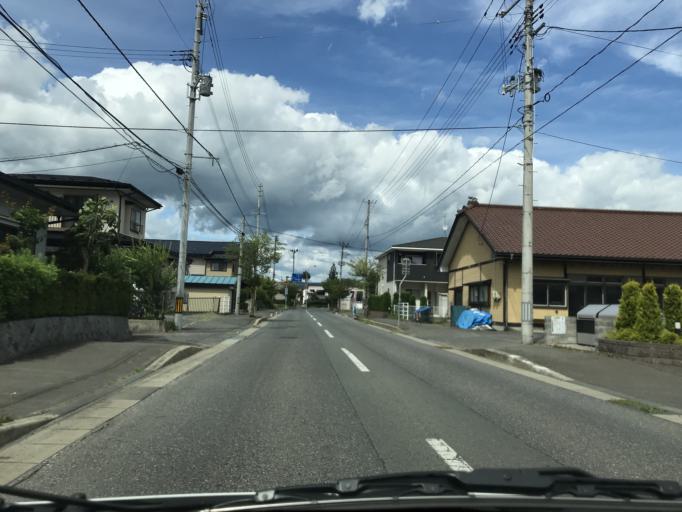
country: JP
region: Iwate
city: Tono
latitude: 39.3254
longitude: 141.5327
